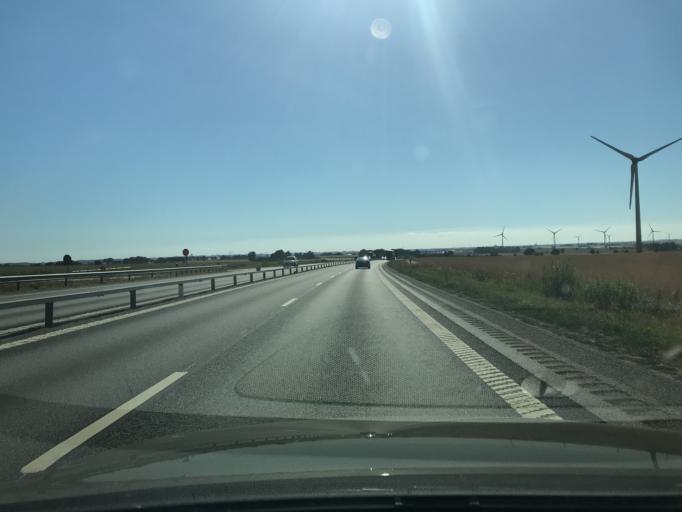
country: SE
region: Skane
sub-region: Hoors Kommun
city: Loberod
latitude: 55.7839
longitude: 13.4105
